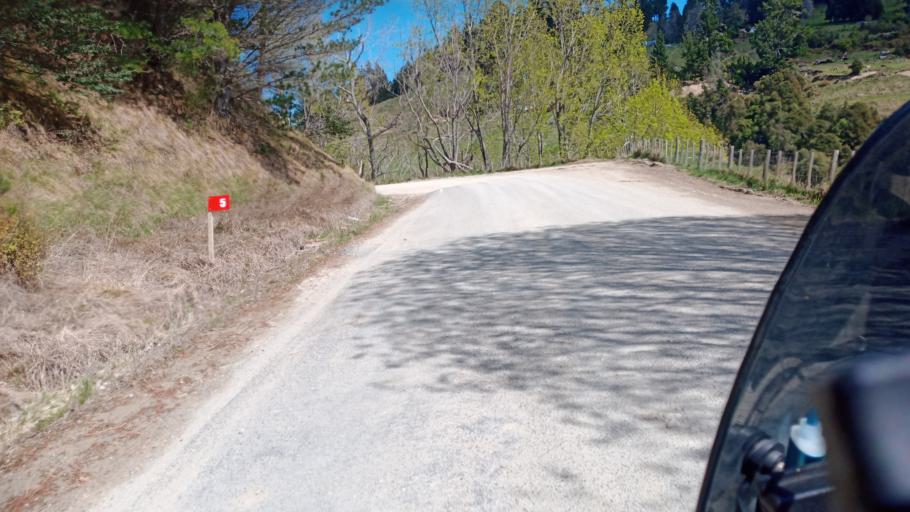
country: NZ
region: Gisborne
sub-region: Gisborne District
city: Gisborne
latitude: -38.8092
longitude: 177.7683
